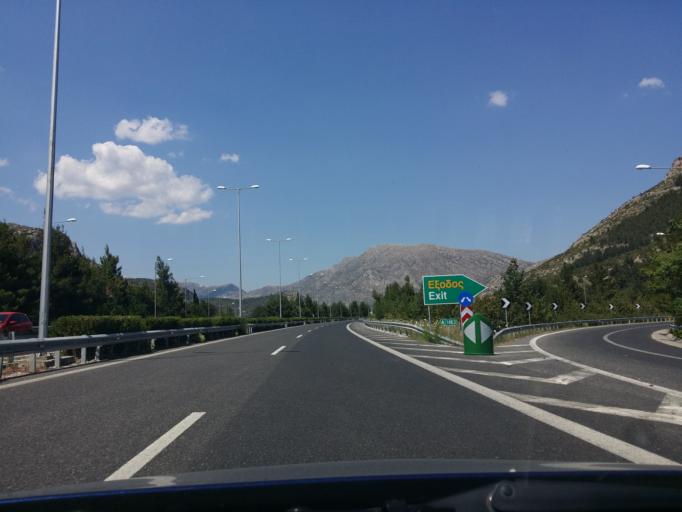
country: GR
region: Peloponnese
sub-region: Nomos Arkadias
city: Tripoli
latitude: 37.5889
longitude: 22.4354
